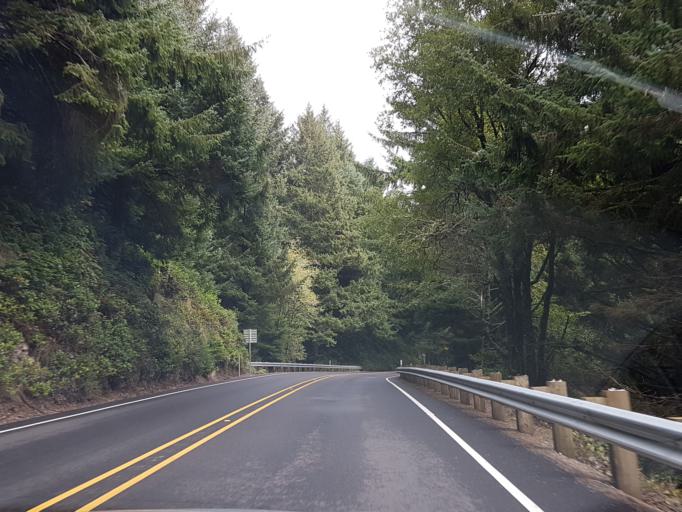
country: US
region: Oregon
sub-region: Lane County
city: Florence
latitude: 44.1197
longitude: -124.1225
